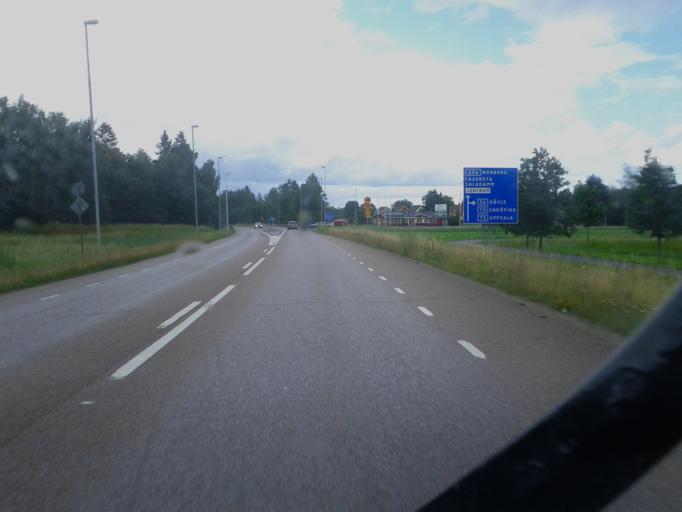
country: SE
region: Vaestmanland
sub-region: Sala Kommun
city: Sala
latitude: 59.9086
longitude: 16.5857
